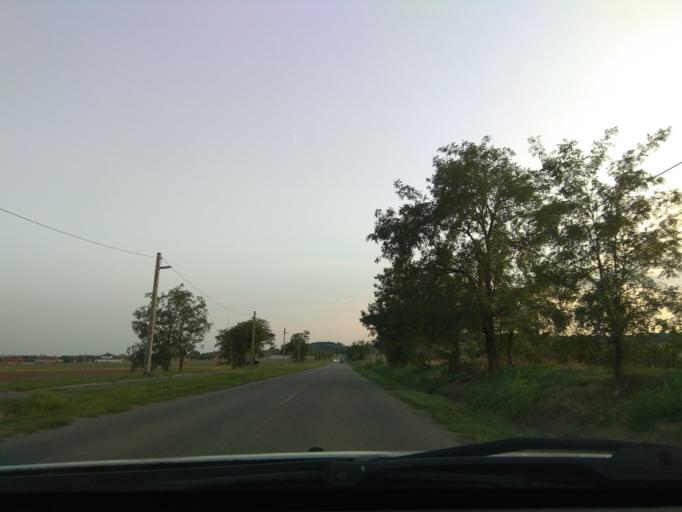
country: HU
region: Borsod-Abauj-Zemplen
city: Szerencs
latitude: 48.1819
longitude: 21.2063
